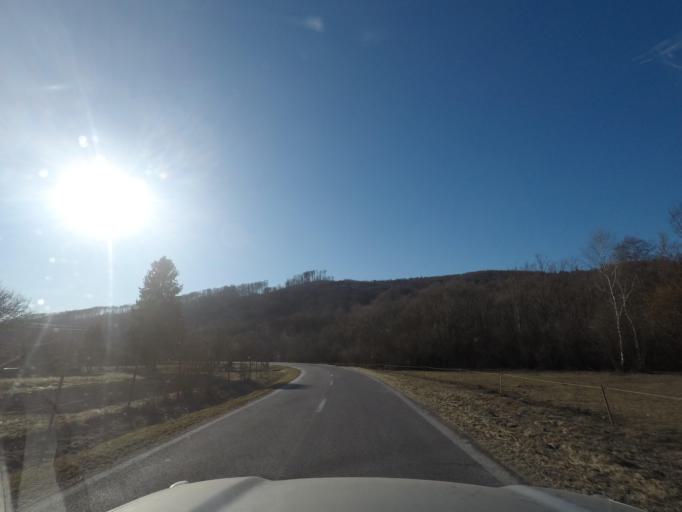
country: SK
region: Presovsky
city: Medzilaborce
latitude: 49.1661
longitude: 22.0248
